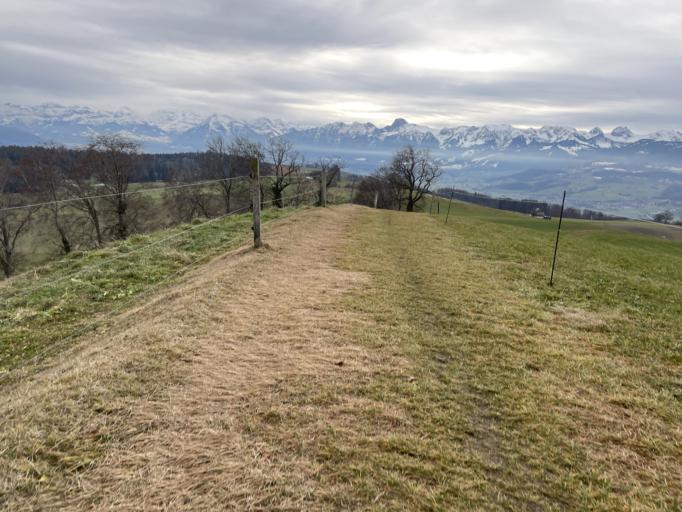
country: CH
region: Bern
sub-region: Bern-Mittelland District
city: Toffen
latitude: 46.8579
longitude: 7.5268
